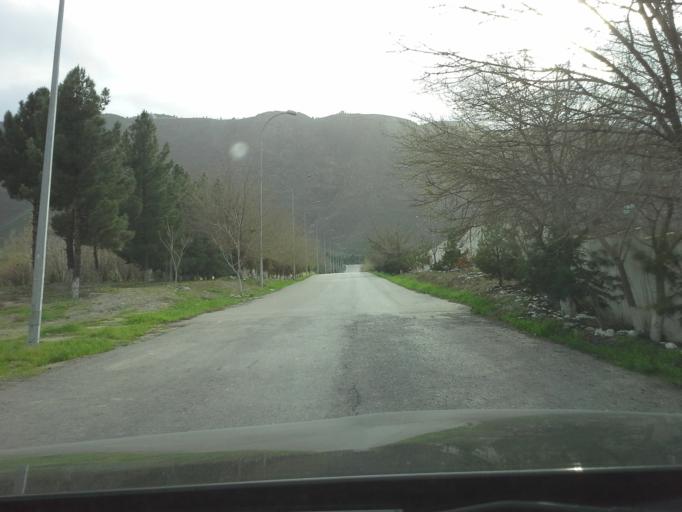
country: TM
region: Ahal
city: Abadan
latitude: 37.9325
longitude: 58.2218
